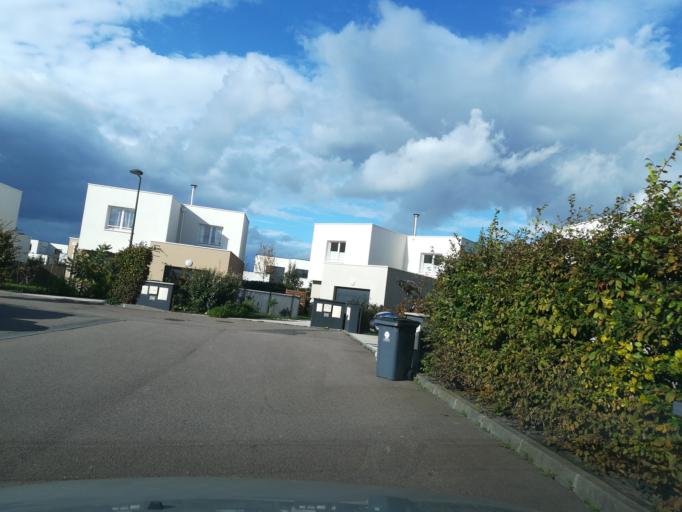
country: FR
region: Haute-Normandie
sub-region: Departement de la Seine-Maritime
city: Bois-Guillaume
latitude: 49.4739
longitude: 1.1294
